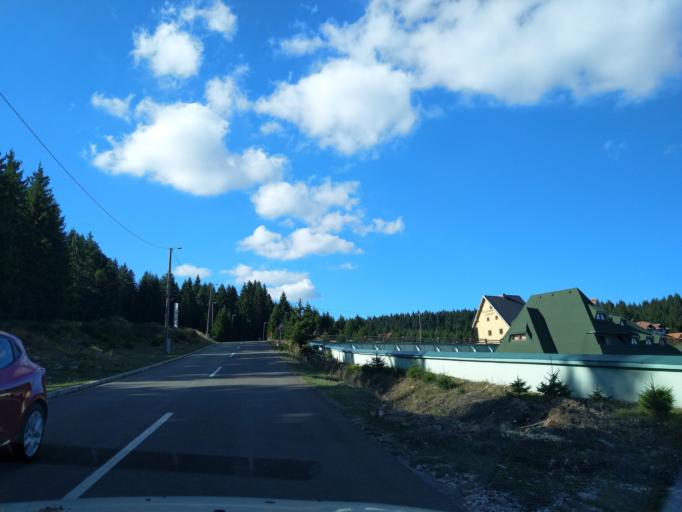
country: RS
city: Sokolovica
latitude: 43.2784
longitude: 20.3384
